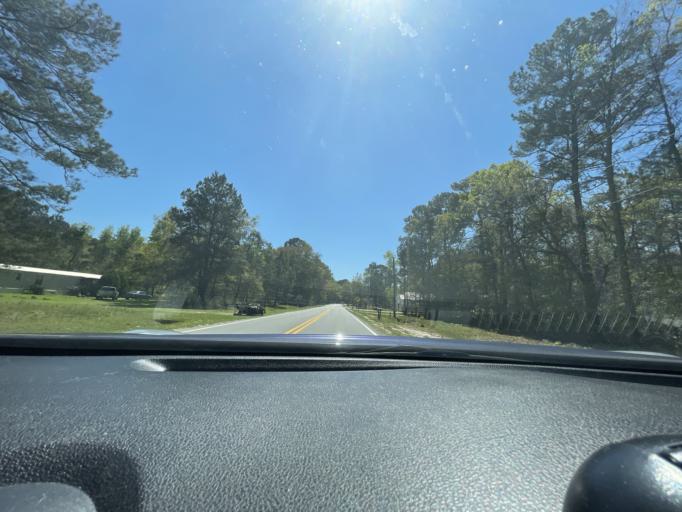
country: US
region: Georgia
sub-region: Chatham County
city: Pooler
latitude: 32.0937
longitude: -81.2399
